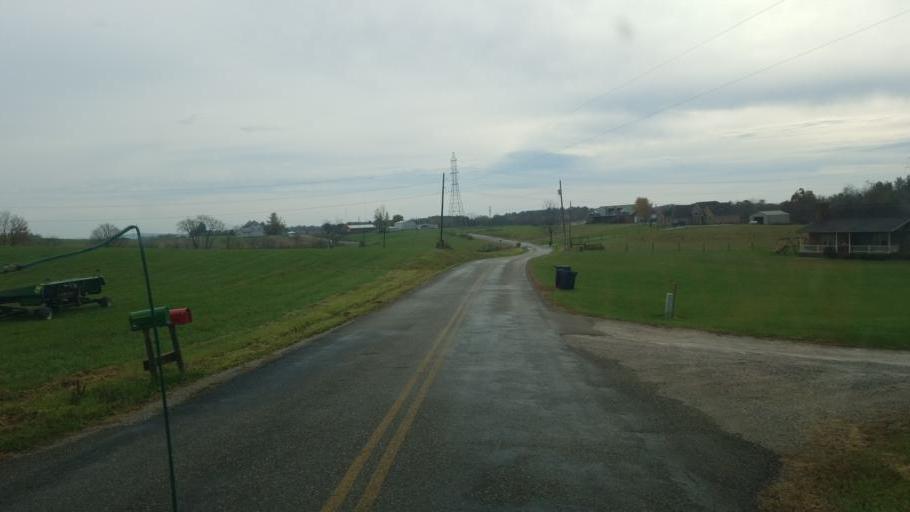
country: US
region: Ohio
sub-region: Washington County
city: Beverly
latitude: 39.5549
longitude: -81.6966
